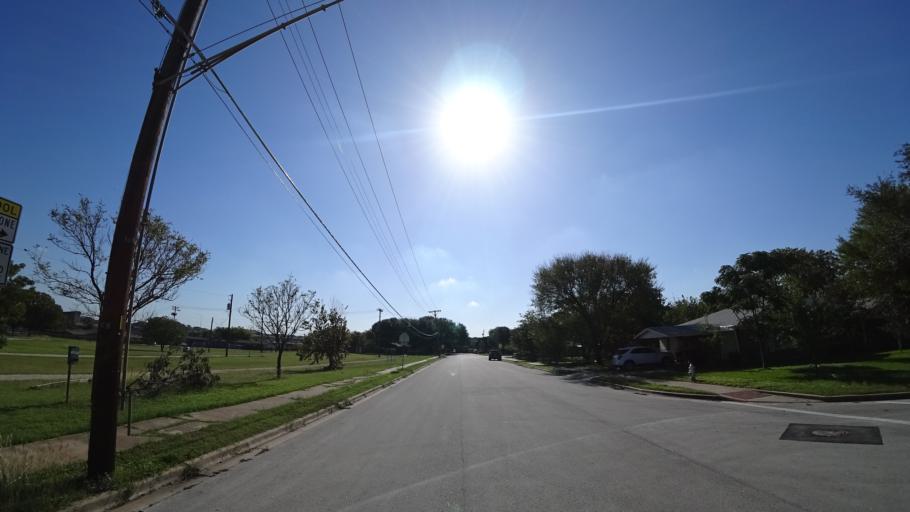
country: US
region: Texas
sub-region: Travis County
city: Austin
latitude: 30.3437
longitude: -97.7098
